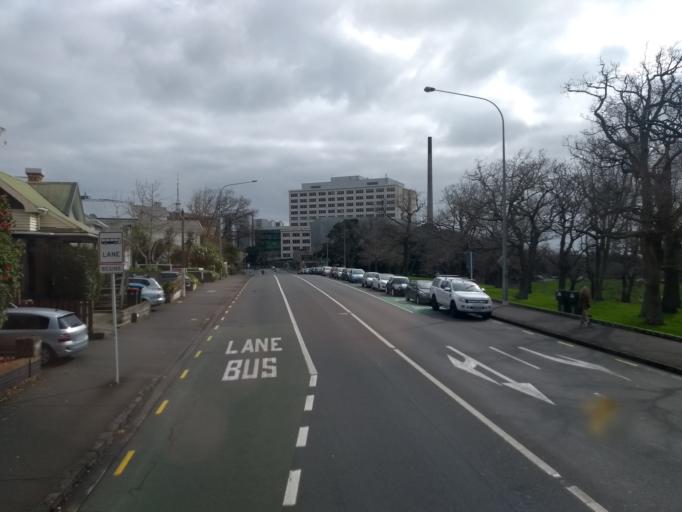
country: NZ
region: Auckland
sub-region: Auckland
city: Auckland
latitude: -36.8638
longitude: 174.7711
